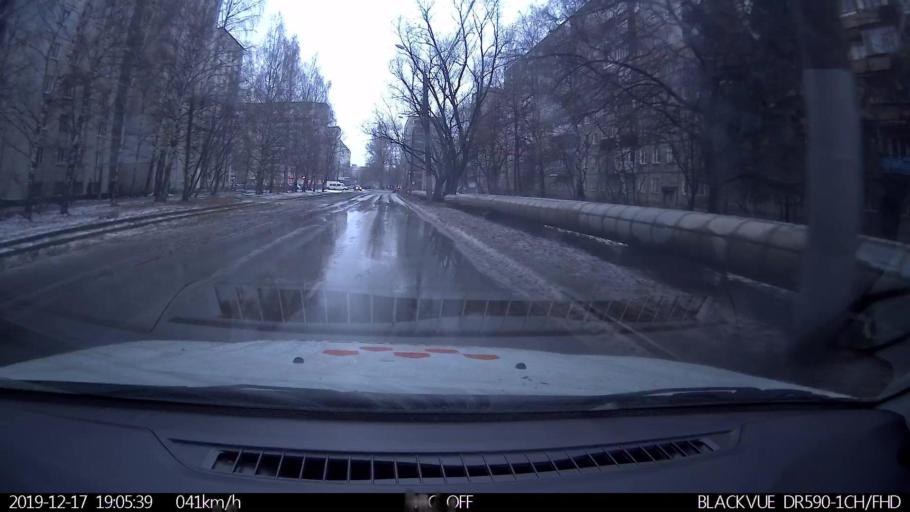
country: RU
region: Nizjnij Novgorod
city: Nizhniy Novgorod
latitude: 56.3350
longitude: 43.8739
